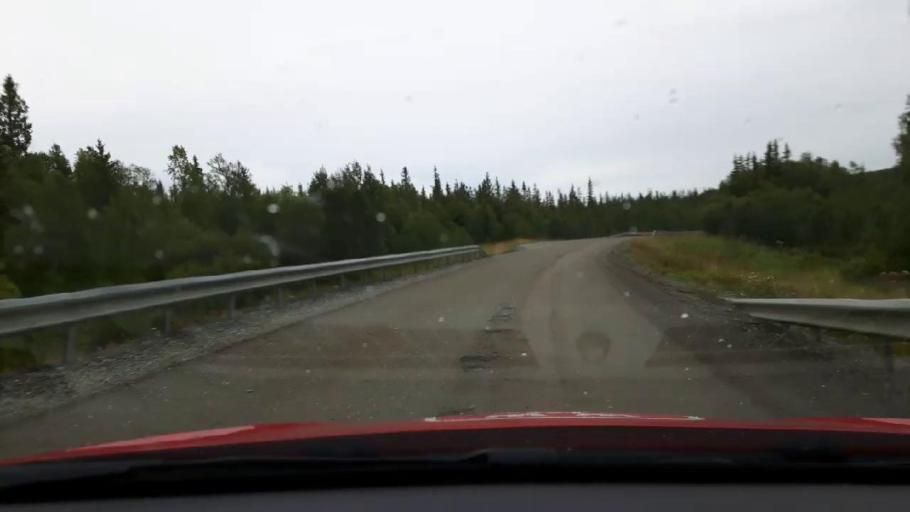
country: NO
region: Nord-Trondelag
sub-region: Meraker
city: Meraker
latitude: 63.5625
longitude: 12.3613
